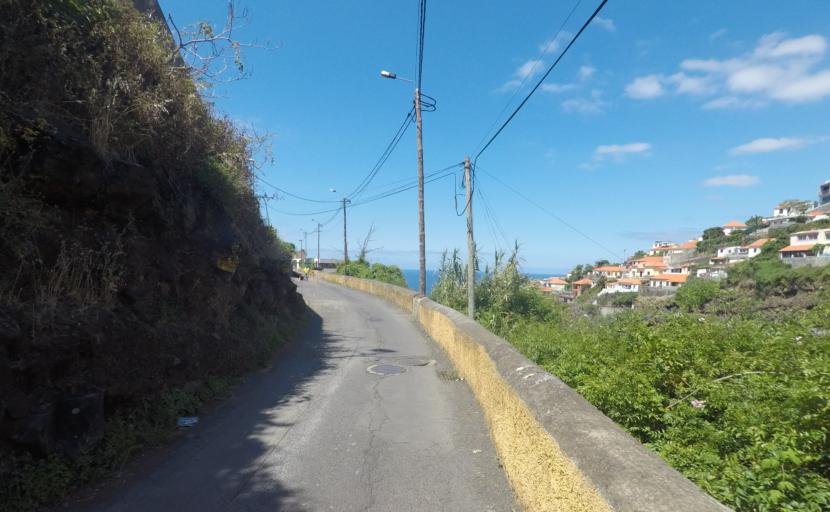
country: PT
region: Madeira
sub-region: Funchal
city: Funchal
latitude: 32.6488
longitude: -16.8862
